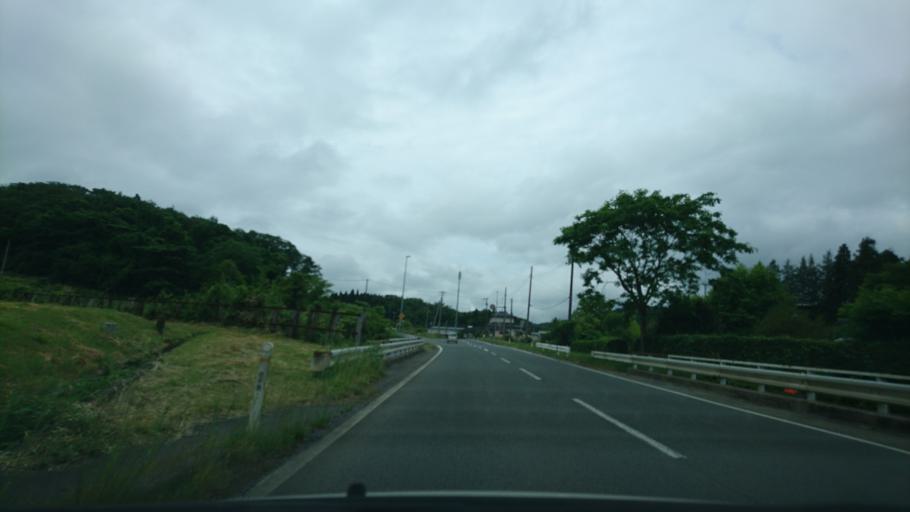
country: JP
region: Iwate
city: Ichinoseki
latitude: 38.8903
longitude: 141.1197
